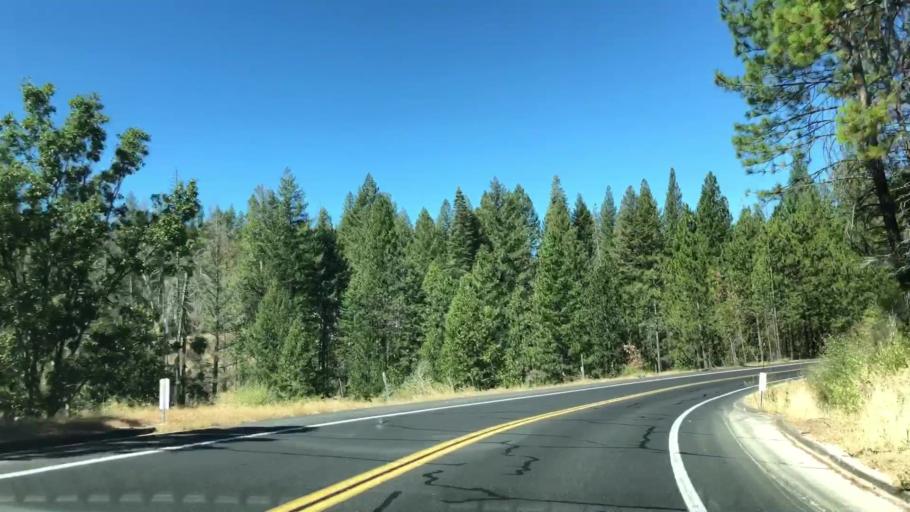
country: US
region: California
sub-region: Mariposa County
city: Midpines
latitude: 37.8184
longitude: -119.9554
